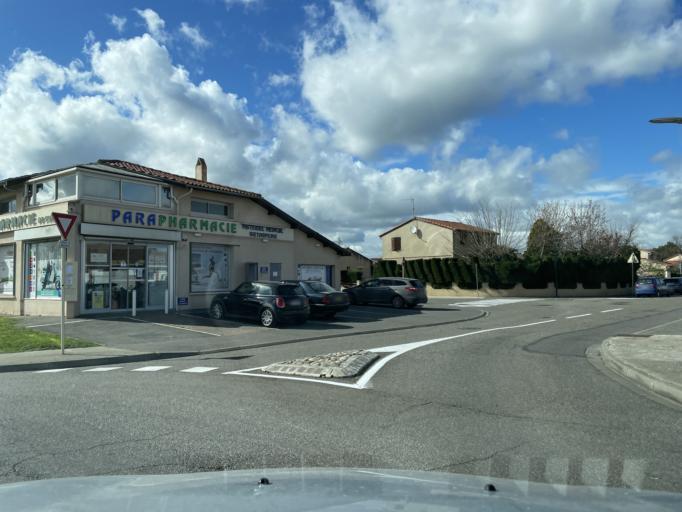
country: FR
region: Midi-Pyrenees
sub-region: Departement de la Haute-Garonne
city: Pibrac
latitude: 43.6158
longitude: 1.2777
